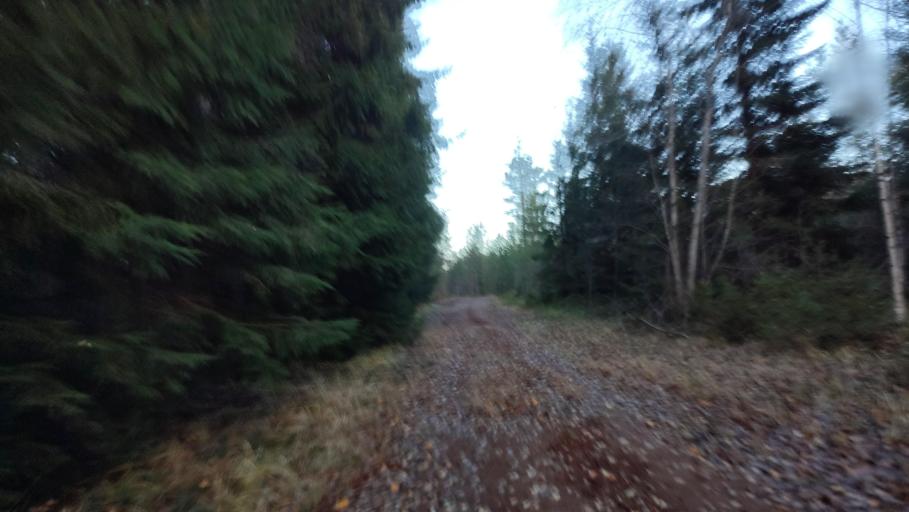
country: FI
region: Southern Ostrobothnia
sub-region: Suupohja
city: Karijoki
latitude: 62.2863
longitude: 21.6282
